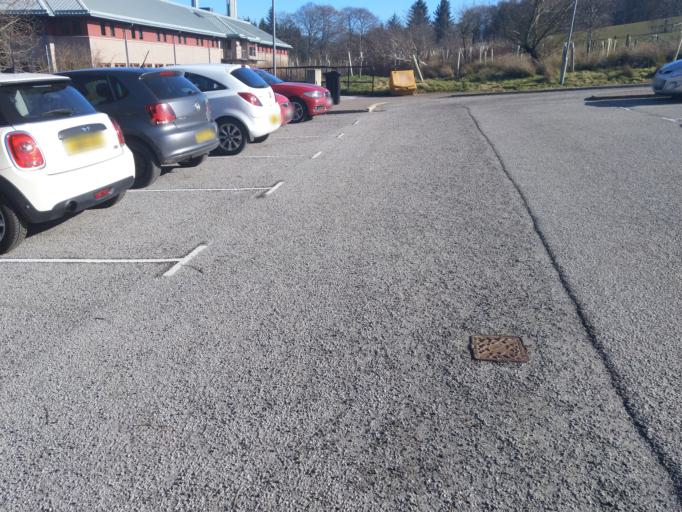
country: GB
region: Scotland
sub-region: Aberdeen City
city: Dyce
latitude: 57.1851
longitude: -2.2144
